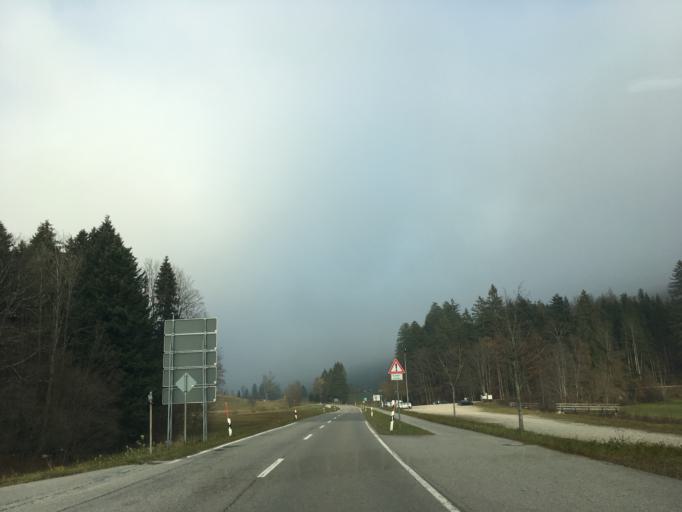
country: AT
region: Tyrol
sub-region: Politischer Bezirk Kufstein
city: Rettenschoss
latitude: 47.6917
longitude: 12.2661
